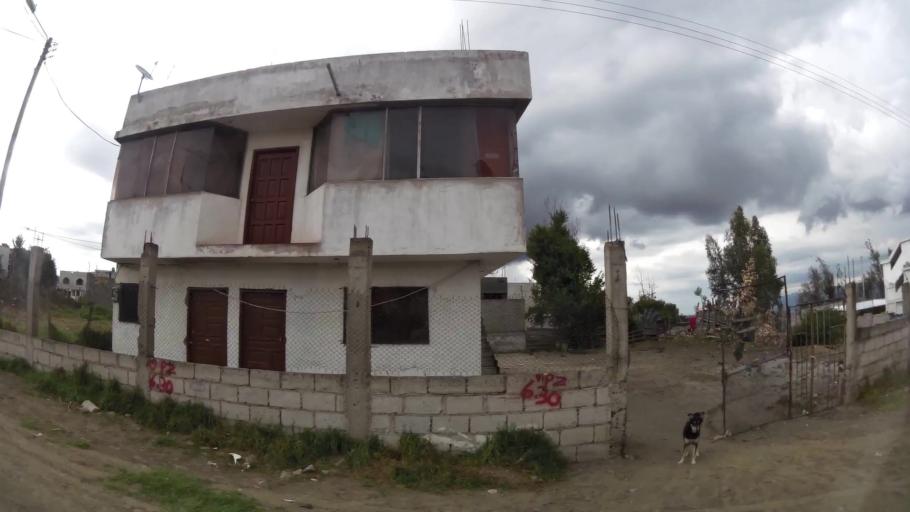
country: EC
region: Tungurahua
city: Ambato
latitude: -1.2695
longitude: -78.6195
